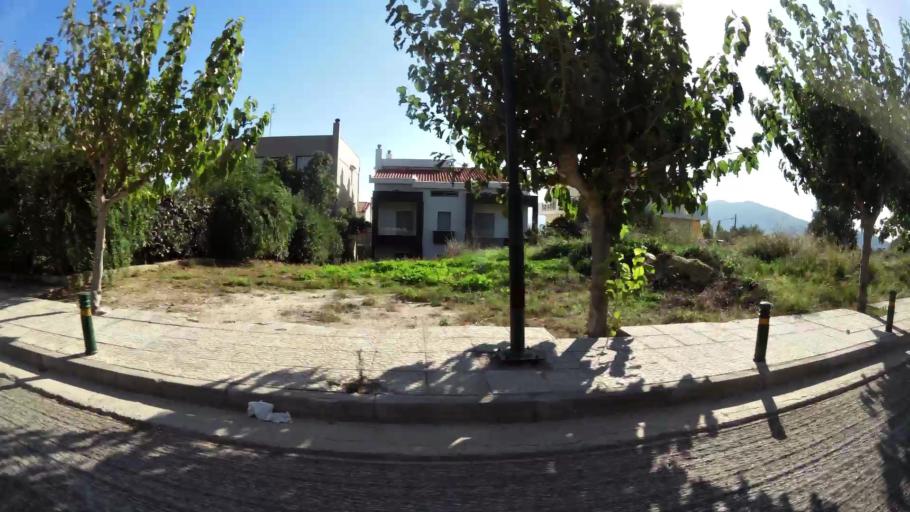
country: GR
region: Attica
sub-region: Nomarchia Anatolikis Attikis
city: Anthousa
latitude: 38.0193
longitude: 23.8740
